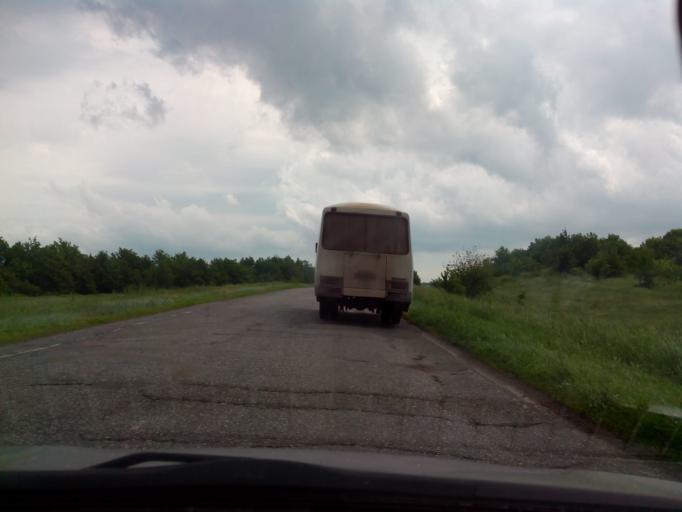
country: RU
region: Volgograd
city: Mikhaylovka
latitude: 49.9669
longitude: 43.0408
